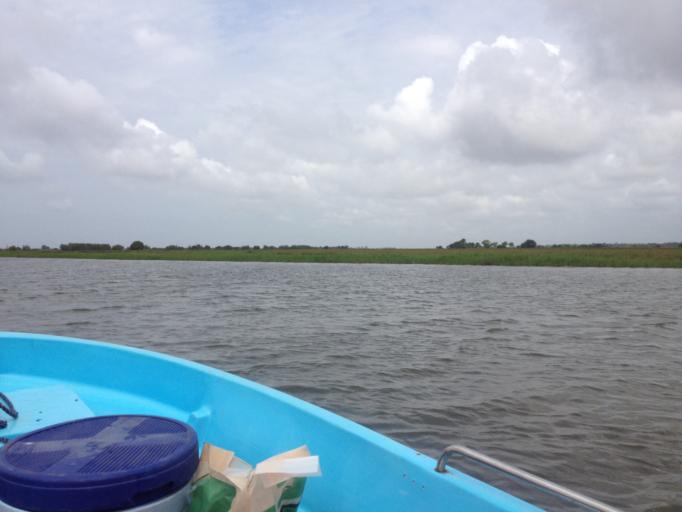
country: BJ
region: Mono
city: Come
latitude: 6.3631
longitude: 1.9410
